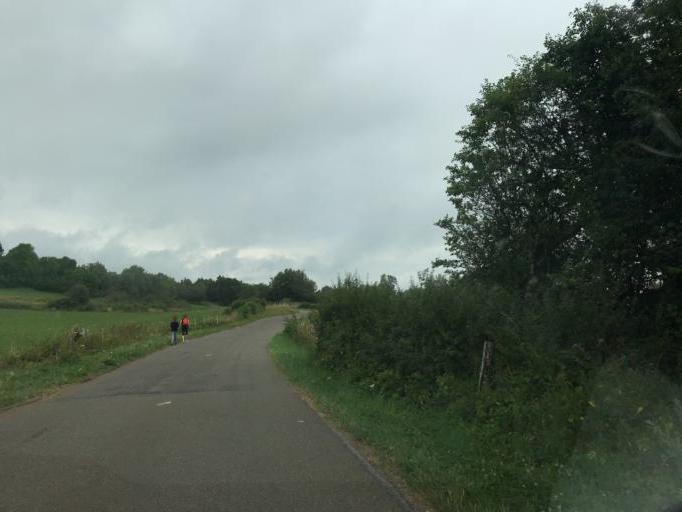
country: FR
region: Rhone-Alpes
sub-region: Departement de l'Ain
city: Arbent
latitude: 46.3146
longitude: 5.7434
